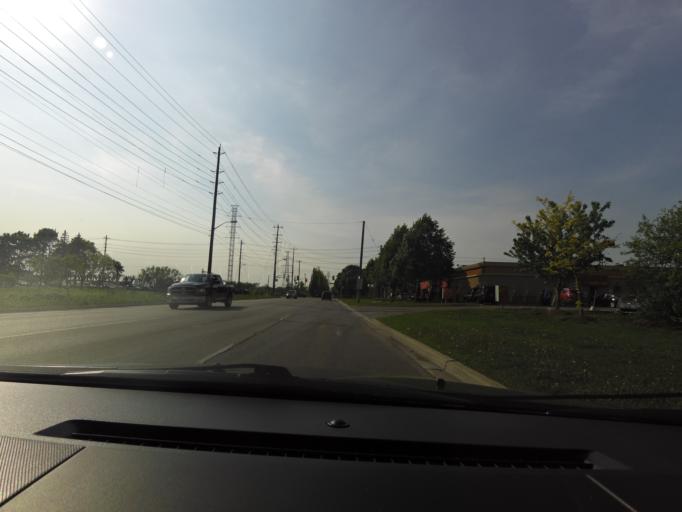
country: CA
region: Ontario
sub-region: Wellington County
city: Guelph
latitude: 43.5574
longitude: -80.2860
